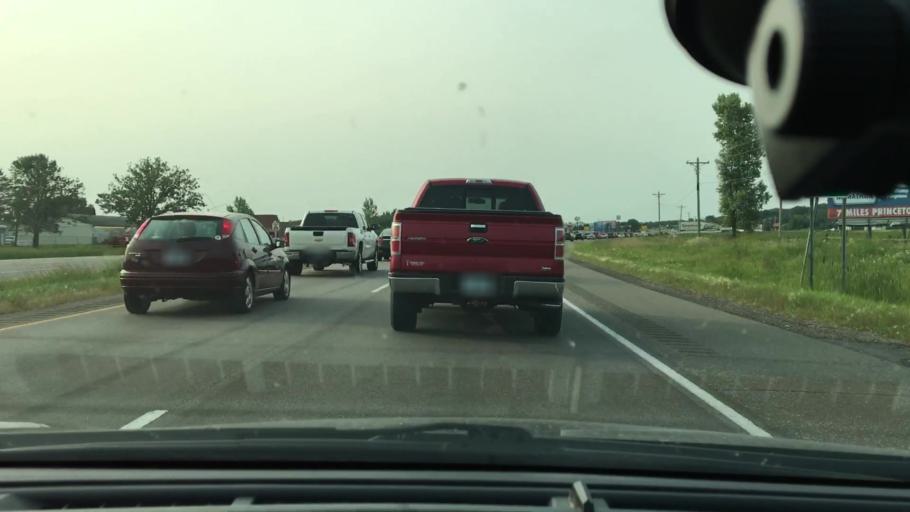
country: US
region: Minnesota
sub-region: Sherburne County
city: Zimmerman
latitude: 45.4383
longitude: -93.5819
